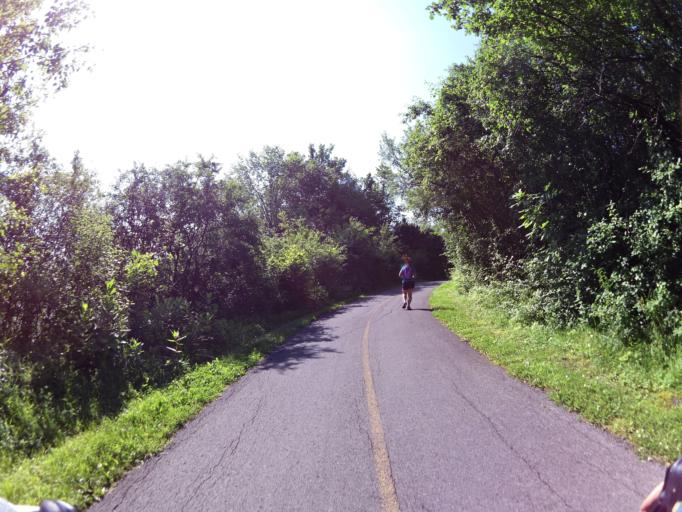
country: CA
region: Quebec
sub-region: Outaouais
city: Gatineau
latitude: 45.4613
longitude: -75.7257
